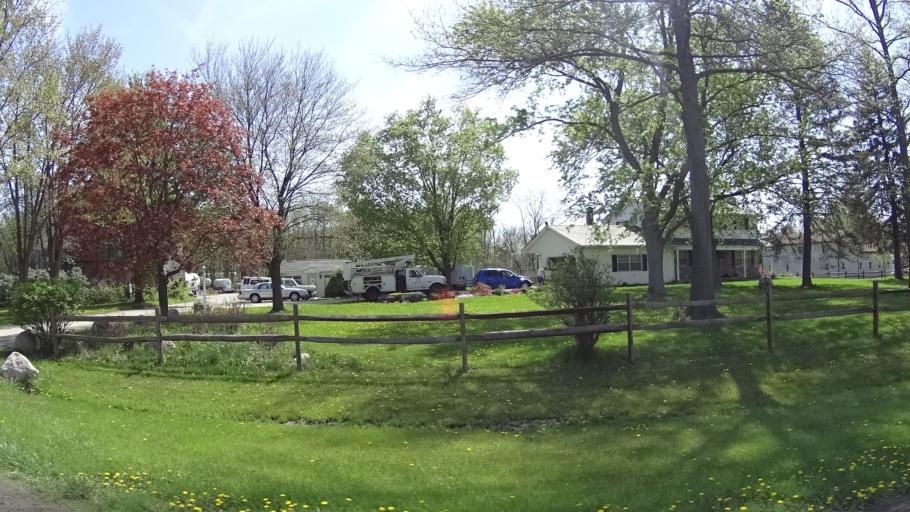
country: US
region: Ohio
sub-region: Lorain County
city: Lagrange
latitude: 41.2754
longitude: -82.1188
